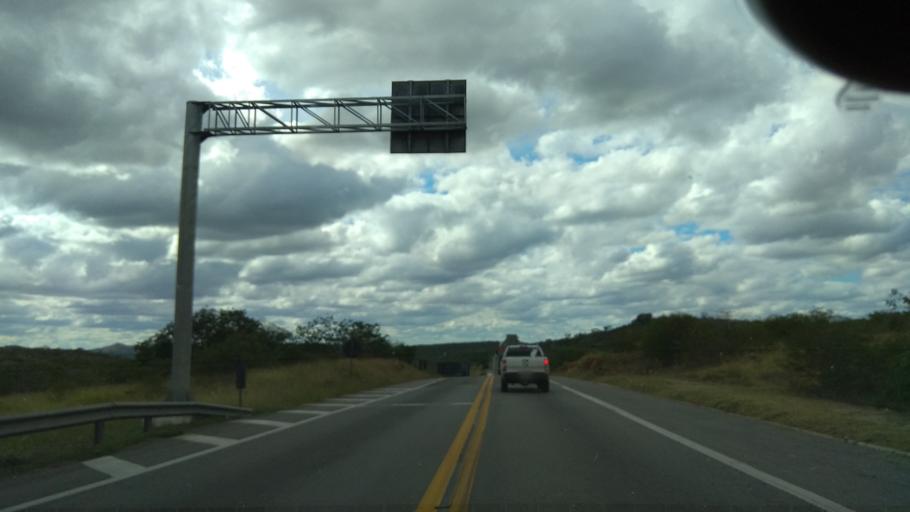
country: BR
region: Bahia
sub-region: Santa Ines
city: Santa Ines
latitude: -13.0060
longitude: -39.9562
